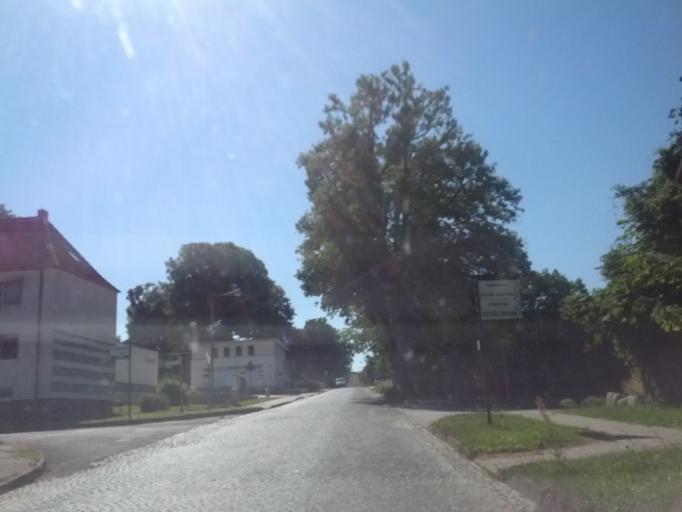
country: DE
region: Mecklenburg-Vorpommern
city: Bergen auf Ruegen
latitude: 54.4224
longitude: 13.4334
